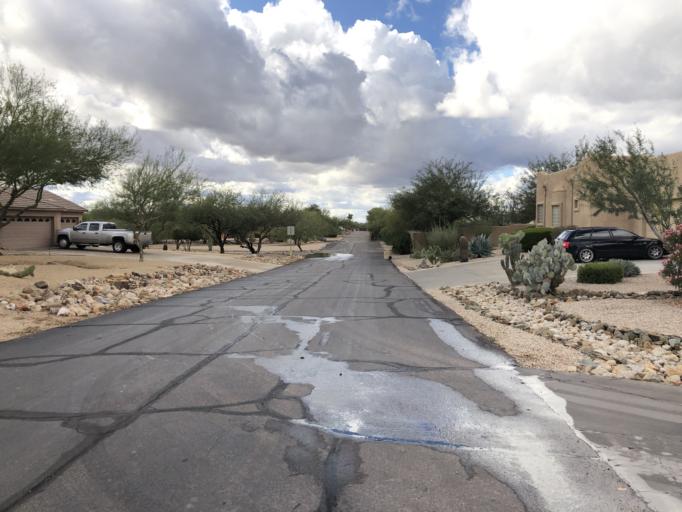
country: US
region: Arizona
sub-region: Maricopa County
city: Anthem
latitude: 33.8390
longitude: -112.0708
